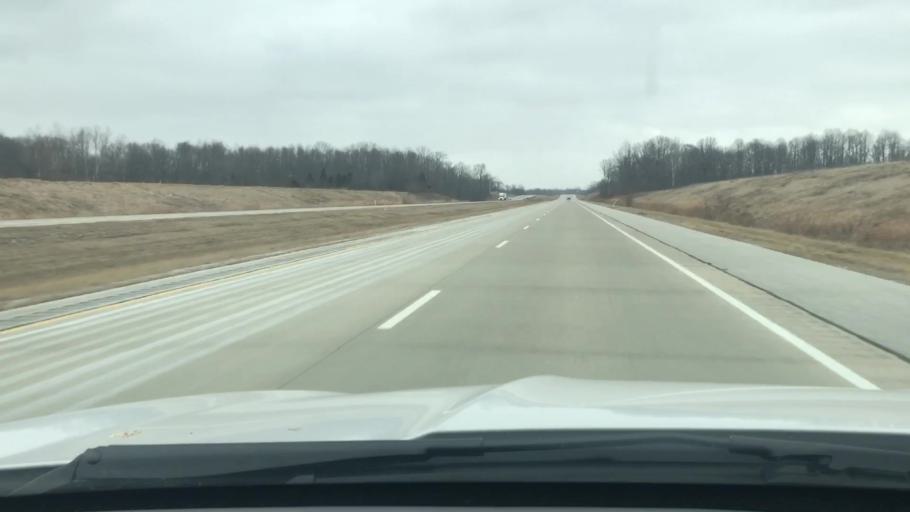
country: US
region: Indiana
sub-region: Carroll County
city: Delphi
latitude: 40.5302
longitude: -86.7103
